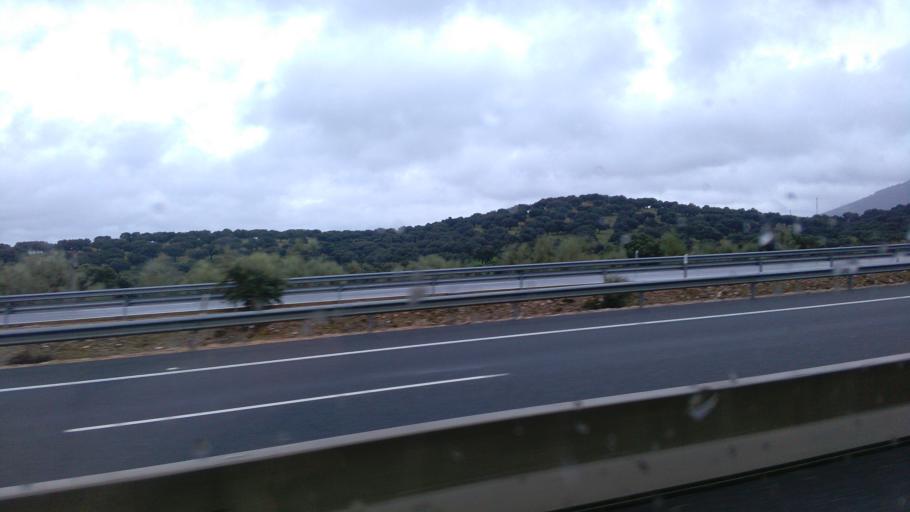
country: ES
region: Extremadura
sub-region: Provincia de Caceres
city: Casas de Miravete
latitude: 39.7635
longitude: -5.7339
